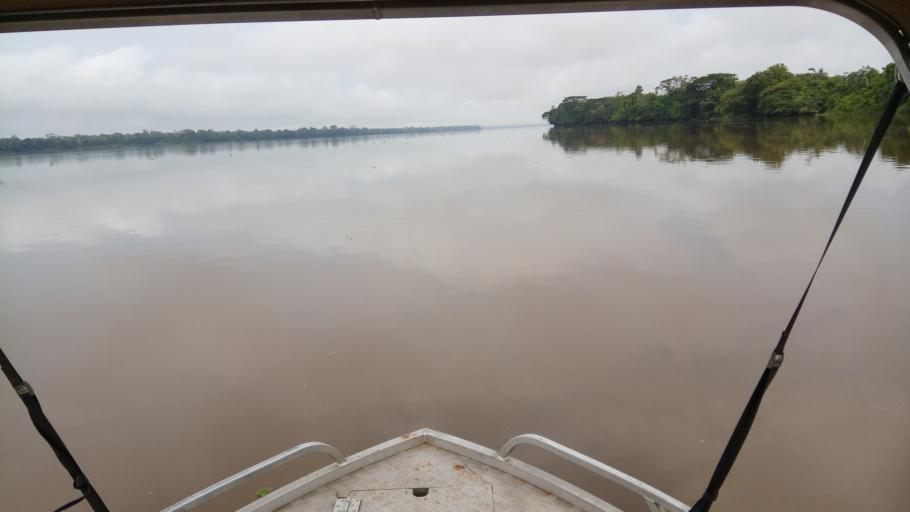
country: CD
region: Eastern Province
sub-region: Sous-Region de la Tshopo
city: Yangambi
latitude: 0.6529
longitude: 24.6442
